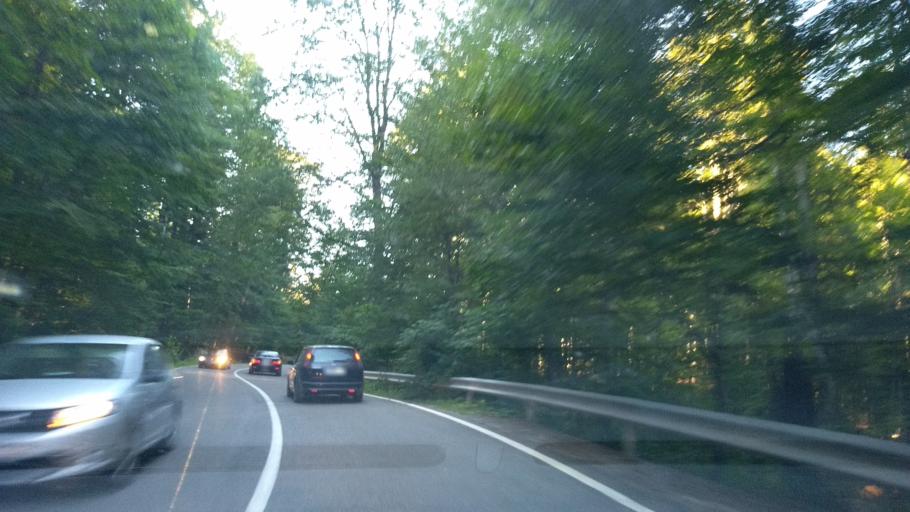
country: RO
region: Prahova
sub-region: Oras Sinaia
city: Sinaia
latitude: 45.3178
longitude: 25.5201
